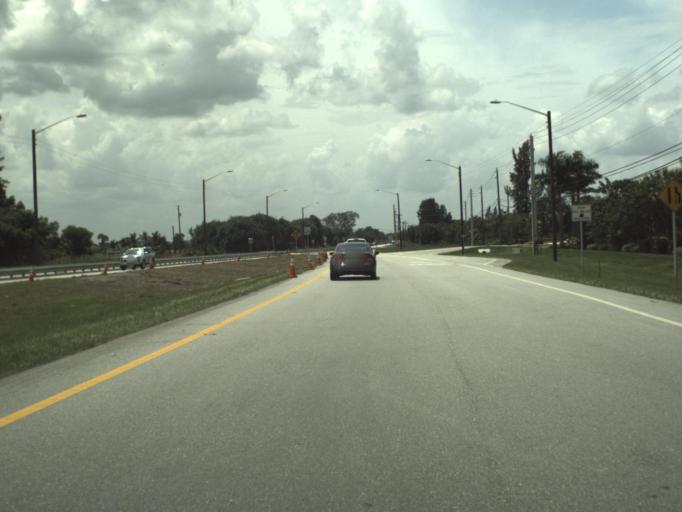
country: US
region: Florida
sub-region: Palm Beach County
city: Villages of Oriole
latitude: 26.4539
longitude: -80.1895
